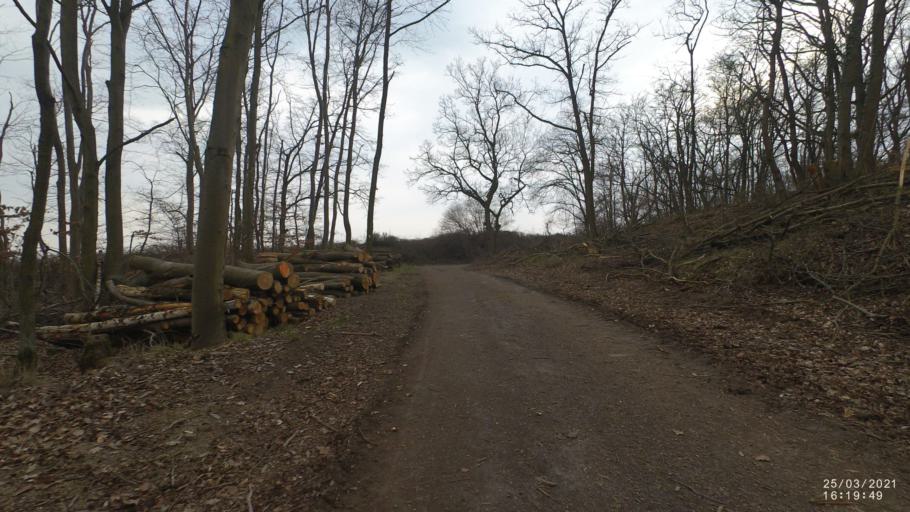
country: DE
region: Rheinland-Pfalz
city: Kottenheim
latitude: 50.3409
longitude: 7.2433
